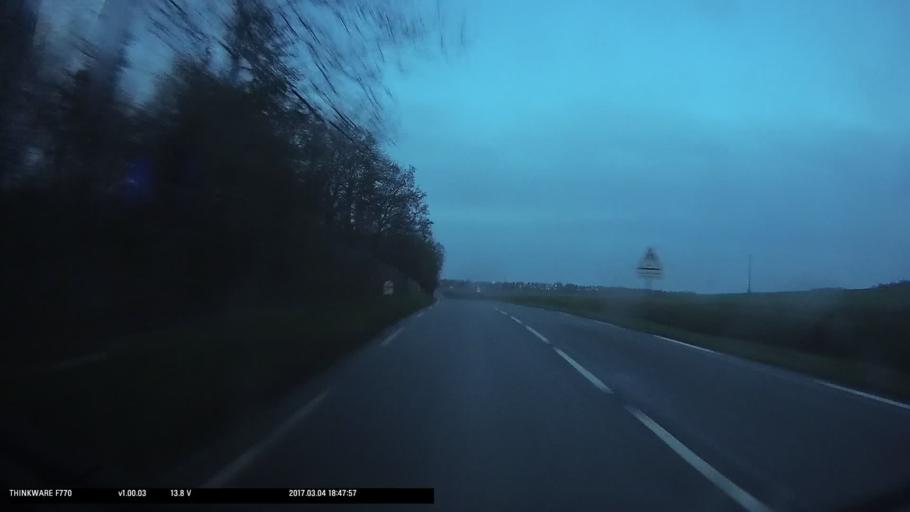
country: FR
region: Ile-de-France
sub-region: Departement du Val-d'Oise
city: Us
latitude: 49.1091
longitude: 1.9755
